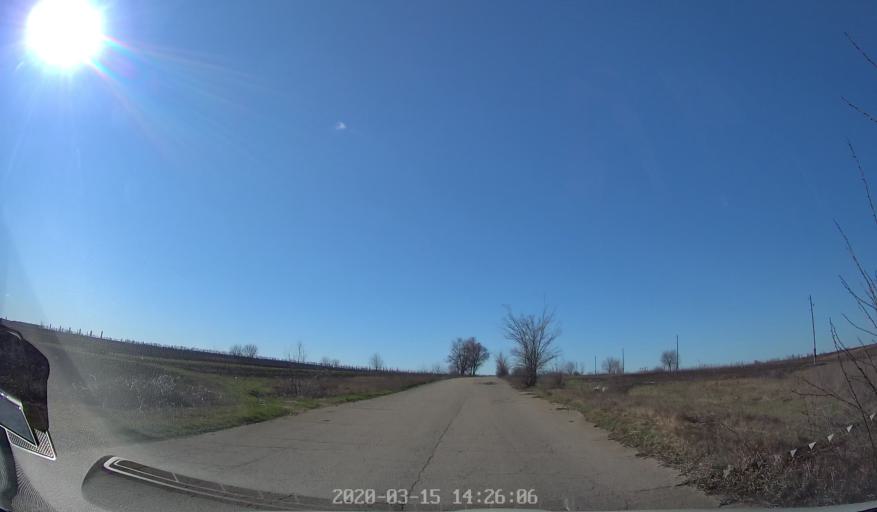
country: MD
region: Orhei
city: Orhei
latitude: 47.3423
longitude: 28.9108
